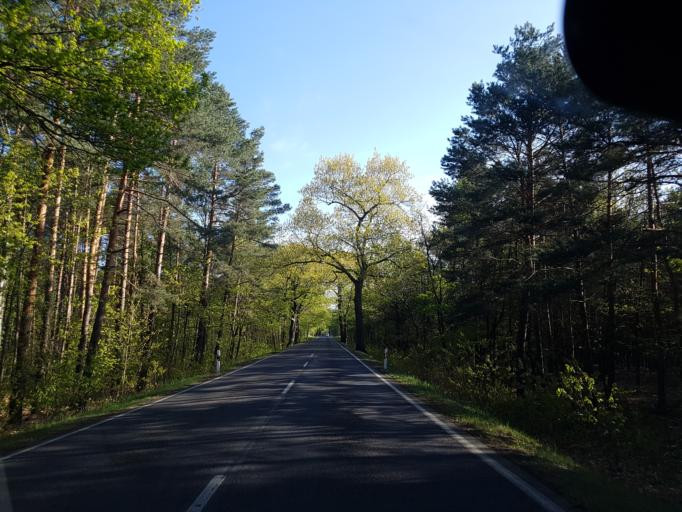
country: DE
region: Brandenburg
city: Grossraschen
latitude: 51.6144
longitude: 14.0222
